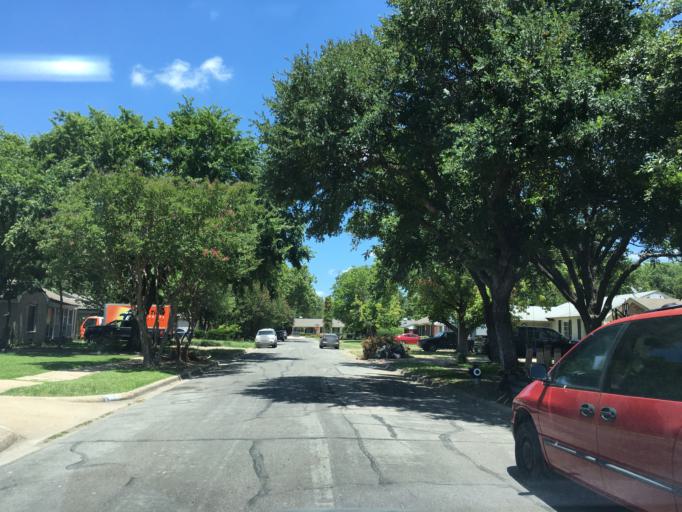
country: US
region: Texas
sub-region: Dallas County
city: Garland
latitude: 32.8484
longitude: -96.6719
